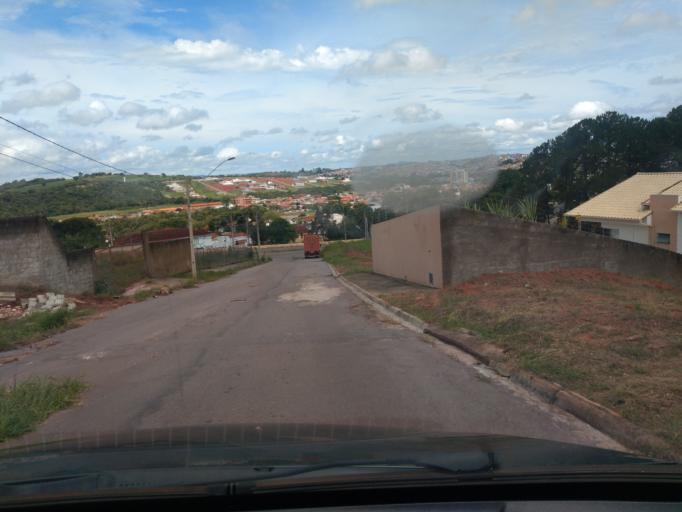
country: BR
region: Minas Gerais
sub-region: Tres Coracoes
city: Tres Coracoes
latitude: -21.6710
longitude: -45.2738
